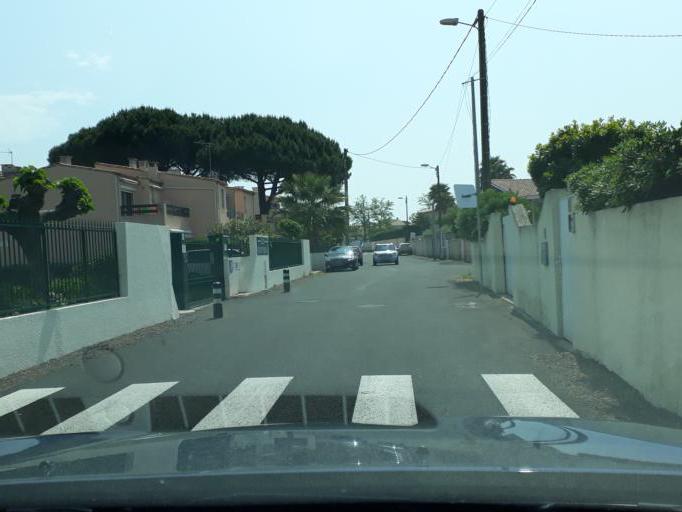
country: FR
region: Languedoc-Roussillon
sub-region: Departement de l'Herault
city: Agde
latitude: 43.2849
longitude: 3.4557
